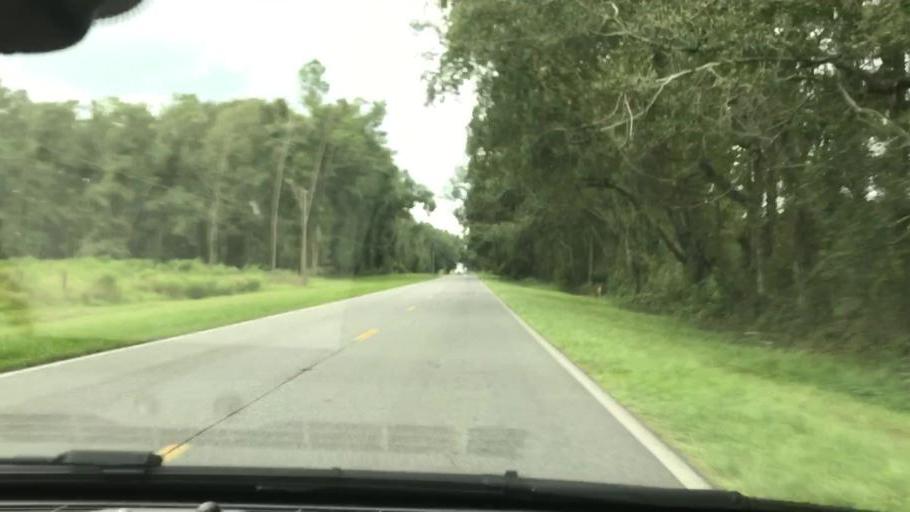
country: US
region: Florida
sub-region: Madison County
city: Madison
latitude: 30.4044
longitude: -83.3004
